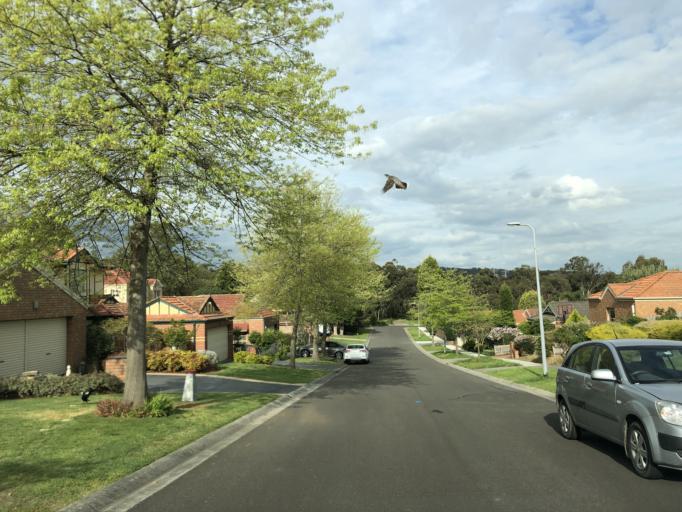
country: AU
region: Victoria
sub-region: Knox
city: Rowville
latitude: -37.9358
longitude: 145.2234
